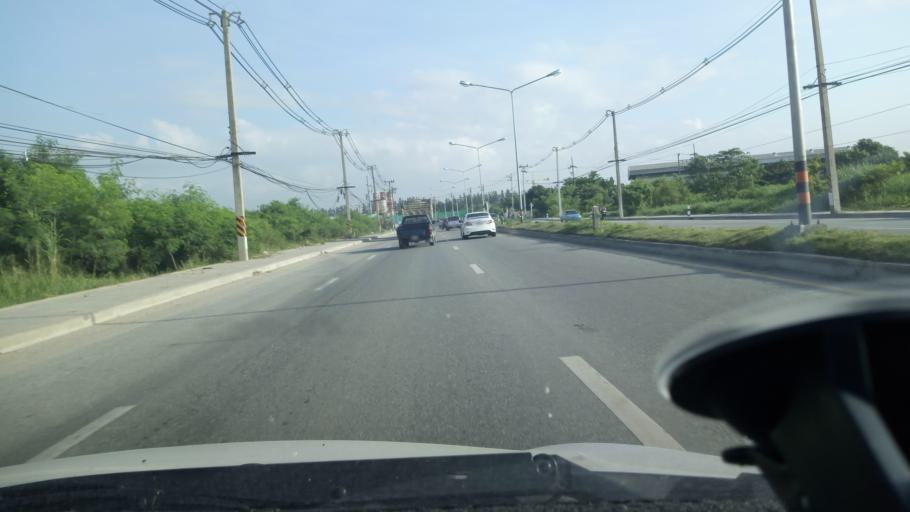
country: TH
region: Chon Buri
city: Phan Thong
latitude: 13.4445
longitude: 101.1032
